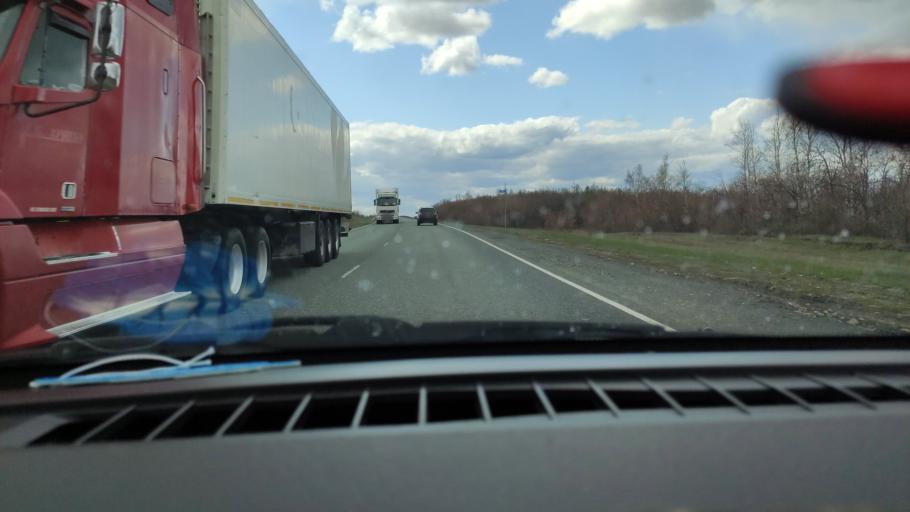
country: RU
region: Saratov
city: Balakovo
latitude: 52.1617
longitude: 47.8226
